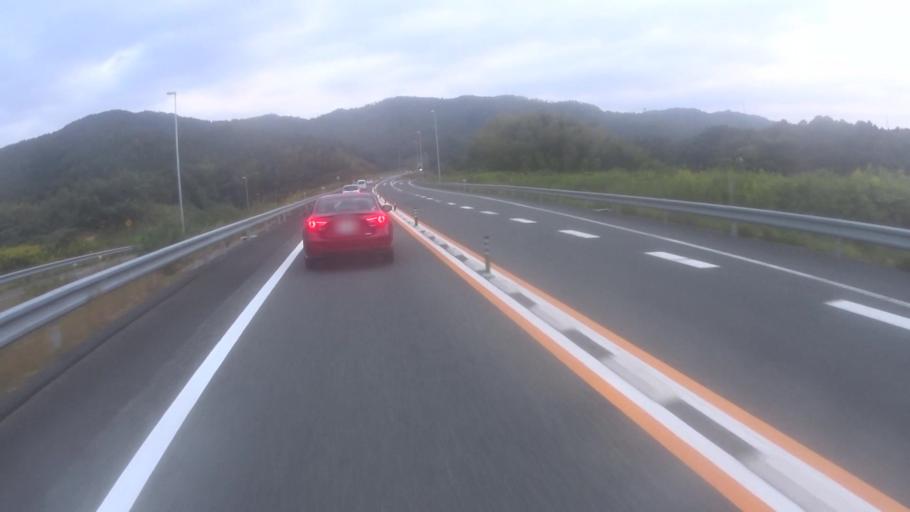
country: JP
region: Kyoto
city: Ayabe
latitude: 35.3374
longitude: 135.3074
